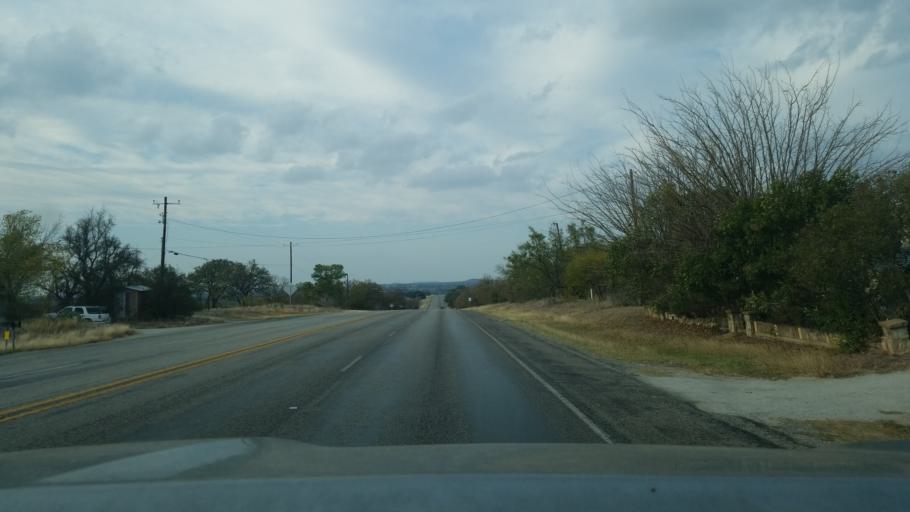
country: US
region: Texas
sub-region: Mills County
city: Goldthwaite
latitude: 31.4902
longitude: -98.5744
